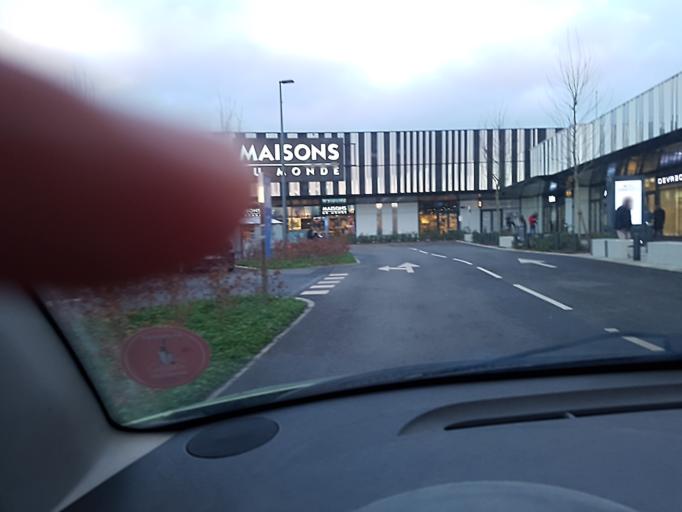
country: FR
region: Nord-Pas-de-Calais
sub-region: Departement du Nord
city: Neuville-en-Ferrain
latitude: 50.7438
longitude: 3.1472
